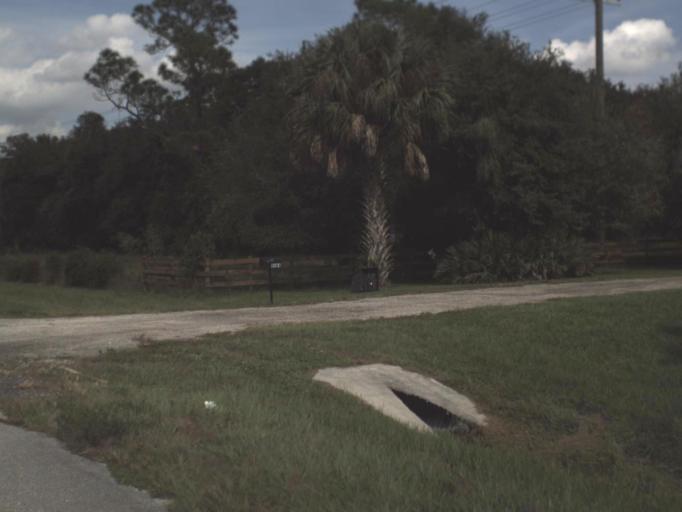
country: US
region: Florida
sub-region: Okeechobee County
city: Cypress Quarters
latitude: 27.3257
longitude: -80.8242
